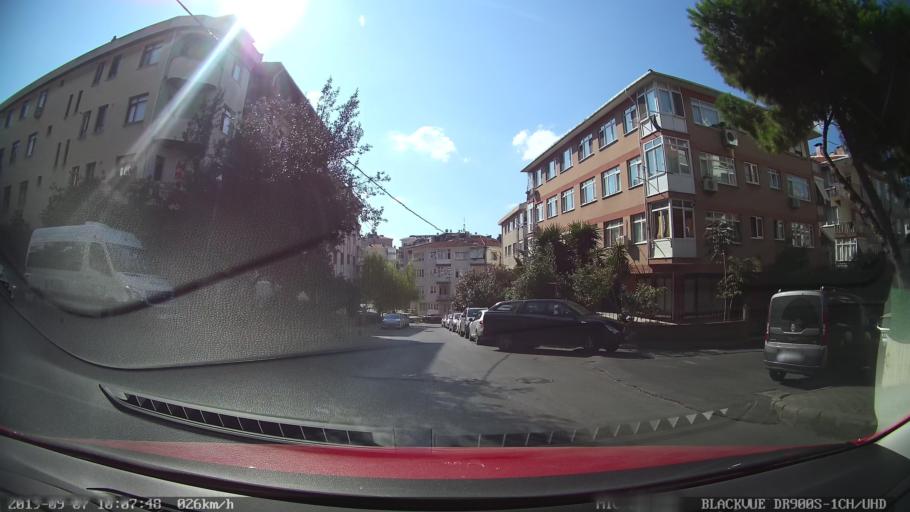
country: TR
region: Istanbul
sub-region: Atasehir
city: Atasehir
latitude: 40.9489
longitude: 29.1124
